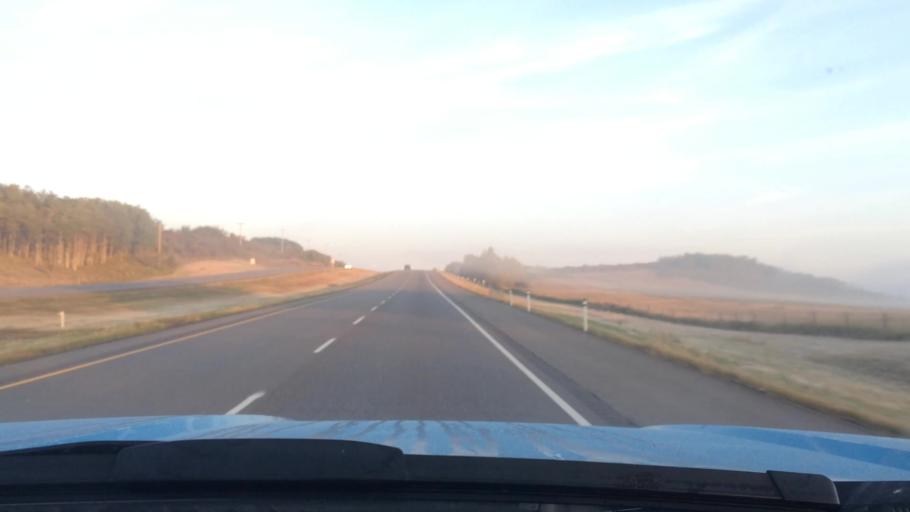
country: CA
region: Alberta
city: Cochrane
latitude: 51.0957
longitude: -114.5913
